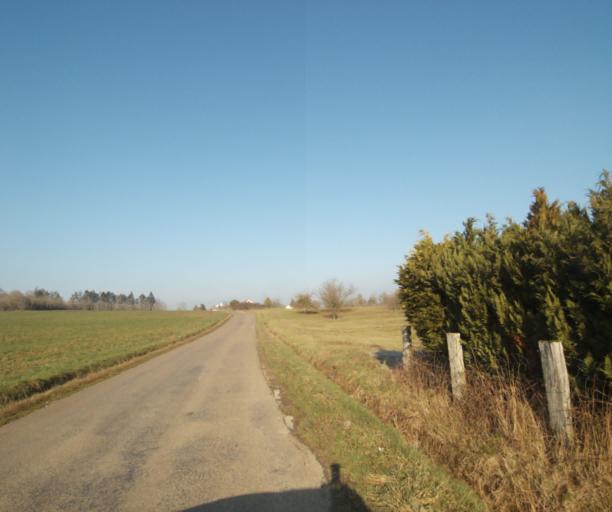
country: FR
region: Champagne-Ardenne
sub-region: Departement de la Haute-Marne
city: Wassy
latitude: 48.5061
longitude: 4.9234
